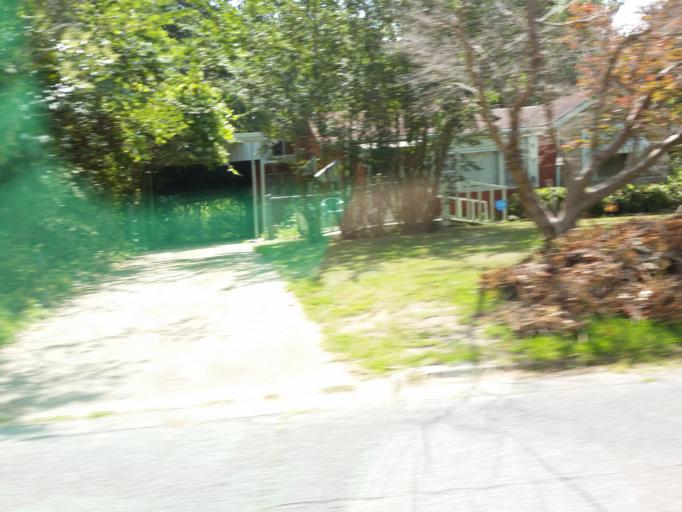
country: US
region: Mississippi
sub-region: Lauderdale County
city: Meridian
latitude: 32.3874
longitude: -88.7168
